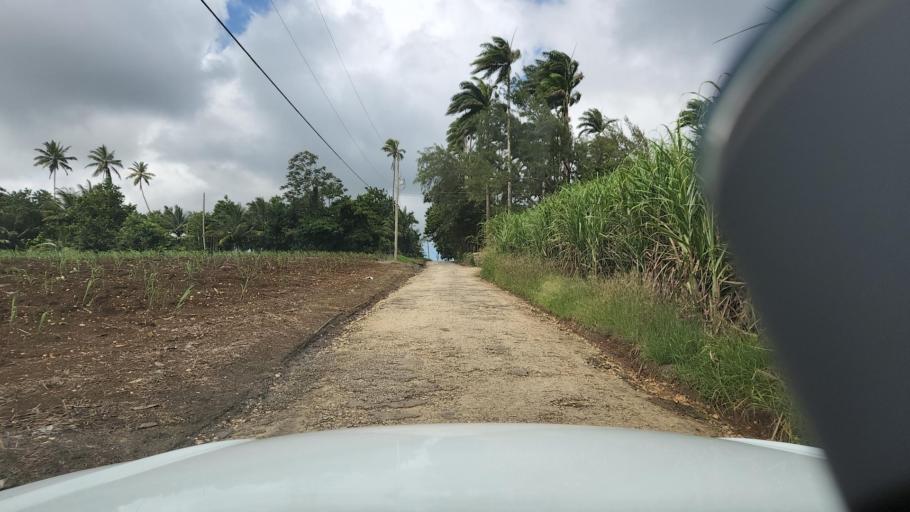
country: BB
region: Saint Joseph
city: Bathsheba
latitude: 13.1957
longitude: -59.5364
